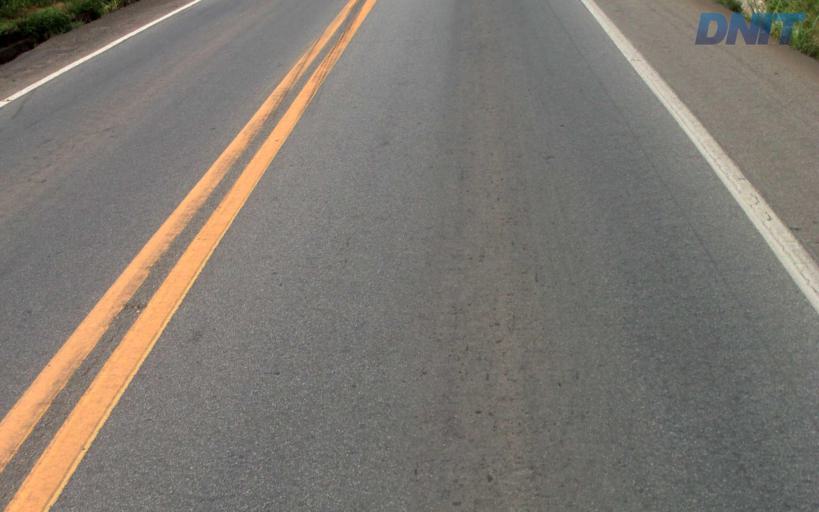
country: BR
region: Minas Gerais
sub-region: Ipaba
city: Ipaba
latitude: -19.3283
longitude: -42.4198
